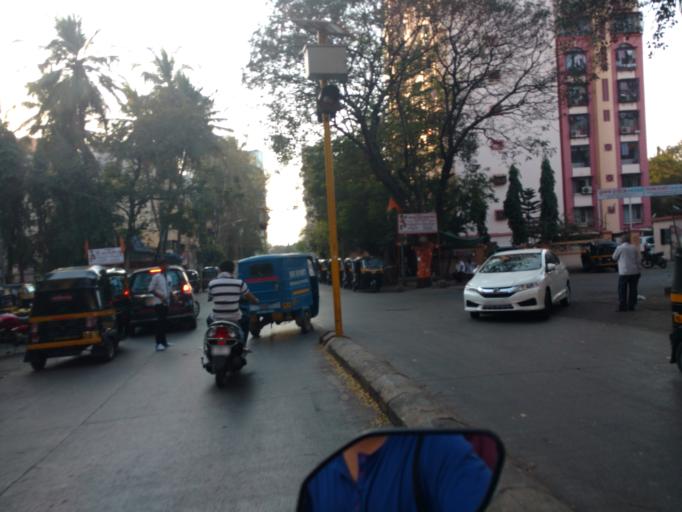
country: IN
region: Maharashtra
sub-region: Mumbai Suburban
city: Borivli
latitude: 19.2034
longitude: 72.8380
